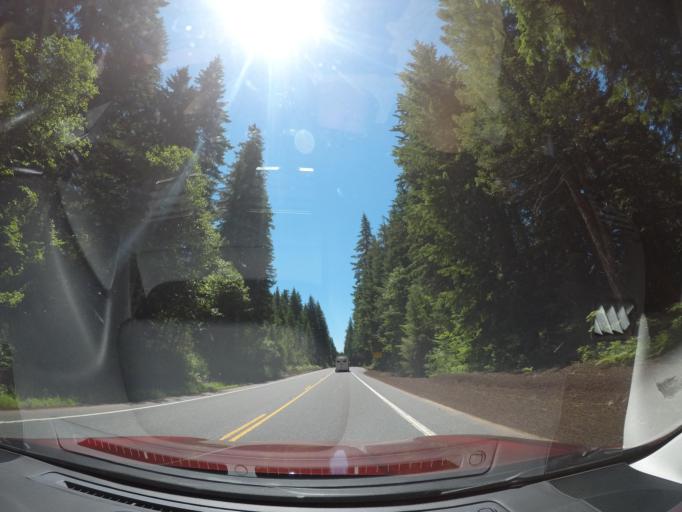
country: US
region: Oregon
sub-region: Deschutes County
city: Sisters
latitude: 44.5316
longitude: -121.9947
